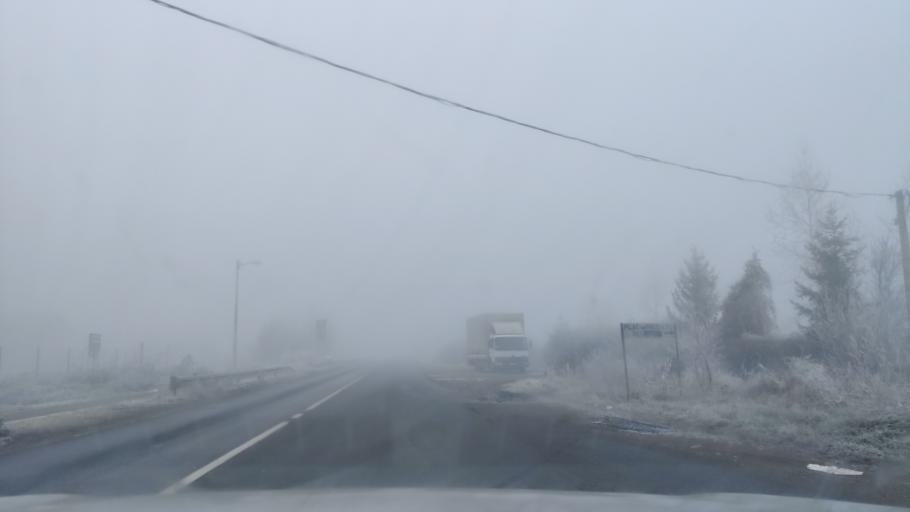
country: RS
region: Central Serbia
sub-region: Belgrade
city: Zemun
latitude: 44.8952
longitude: 20.4557
